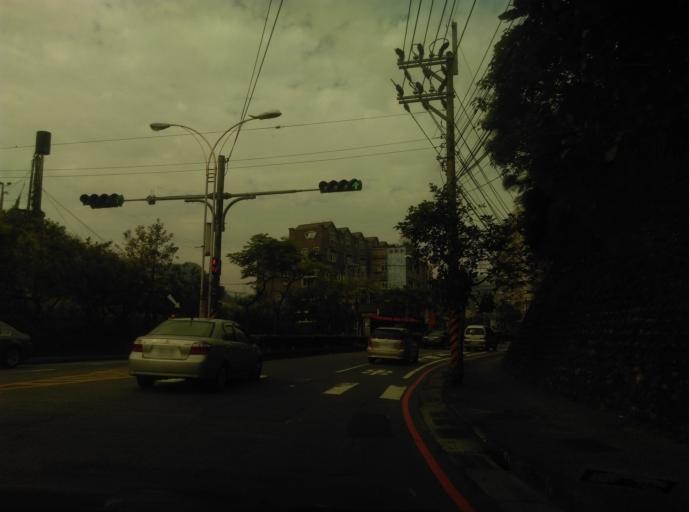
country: TW
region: Taiwan
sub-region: Keelung
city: Keelung
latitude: 25.1523
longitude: 121.6975
